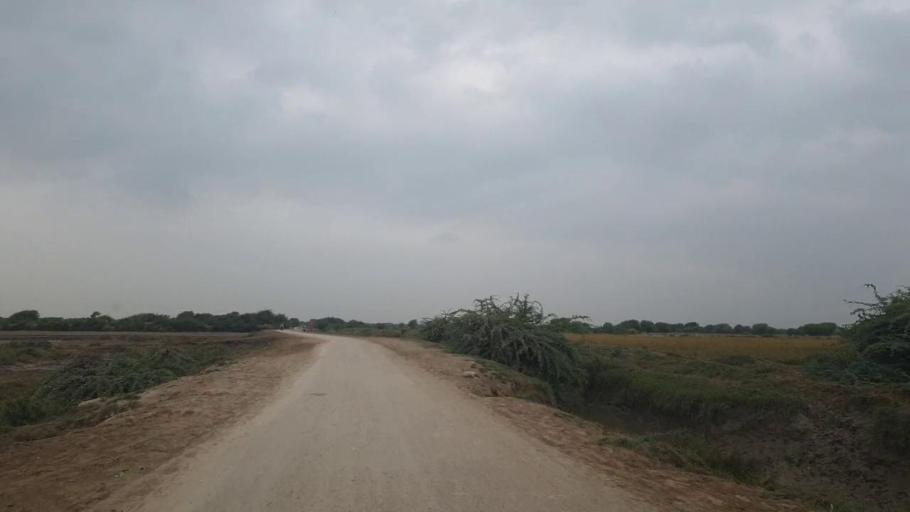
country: PK
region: Sindh
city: Badin
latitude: 24.6415
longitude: 68.6815
